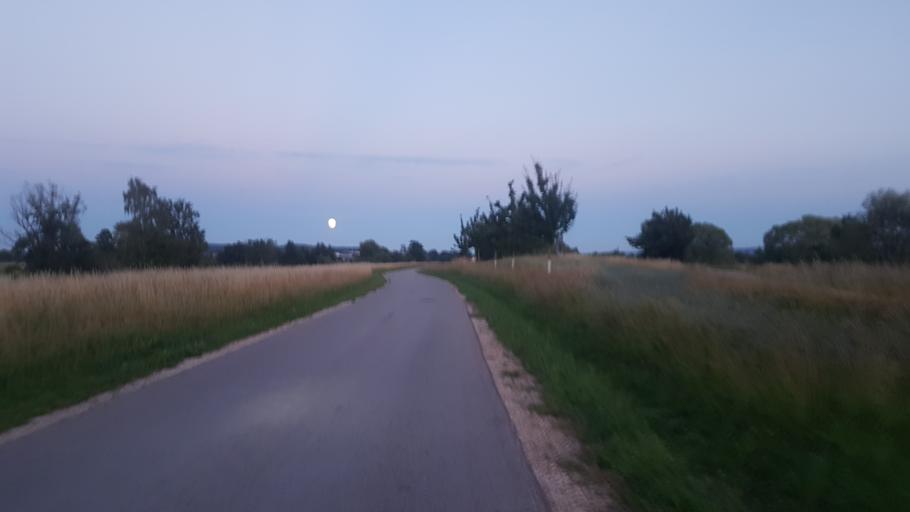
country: DE
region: Bavaria
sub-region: Regierungsbezirk Mittelfranken
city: Muhr am See
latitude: 49.1414
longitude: 10.7311
